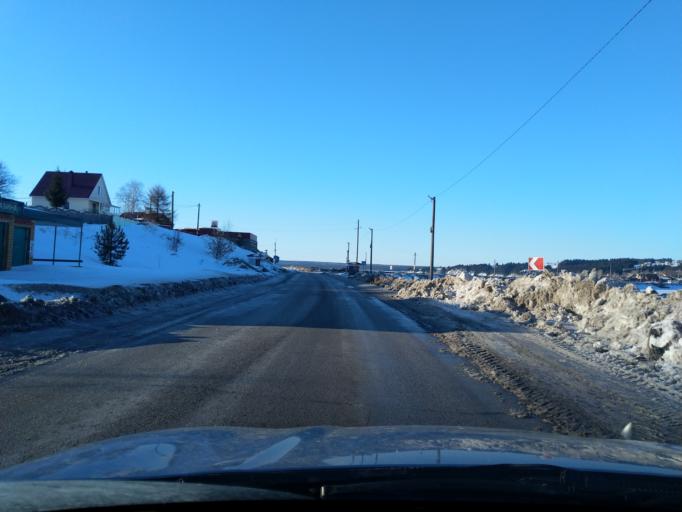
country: RU
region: Perm
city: Polazna
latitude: 58.3004
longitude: 56.4193
